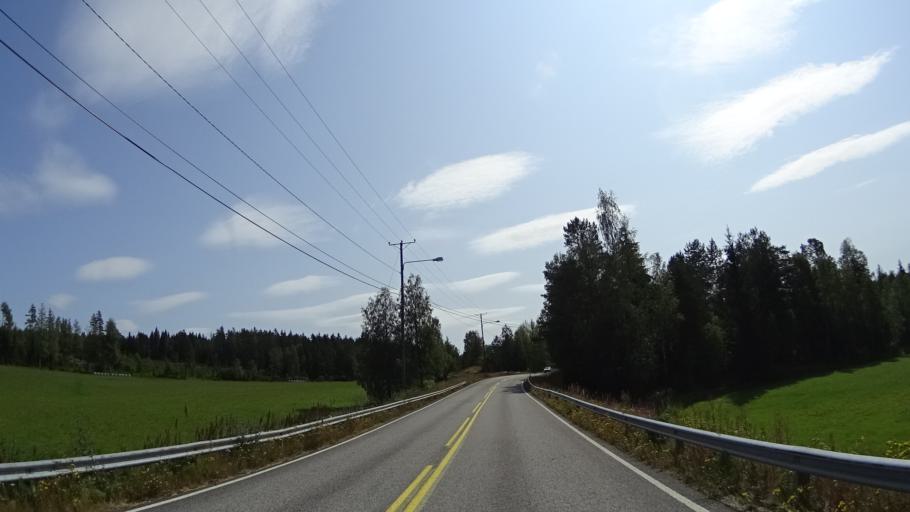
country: FI
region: Pirkanmaa
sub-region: Ylae-Pirkanmaa
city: Maenttae
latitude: 61.9088
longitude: 24.7845
